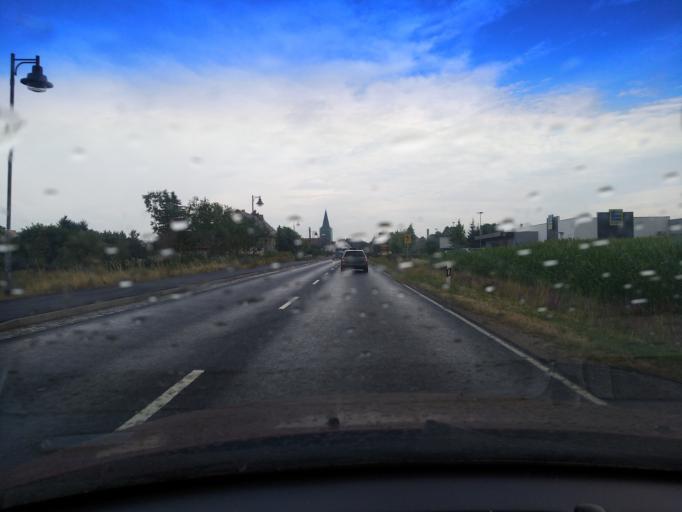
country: DE
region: Saxony
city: Kodersdorf
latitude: 51.2344
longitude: 14.8911
